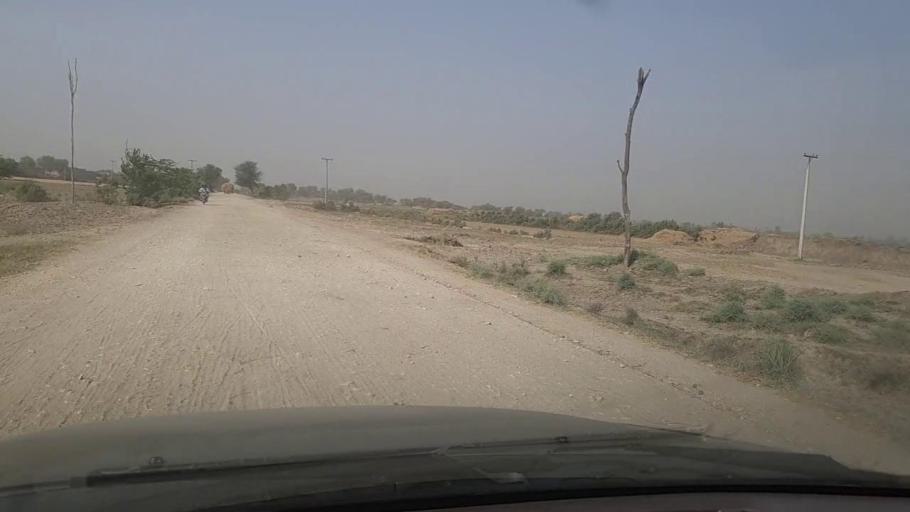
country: PK
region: Sindh
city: Shikarpur
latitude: 27.8997
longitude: 68.5903
